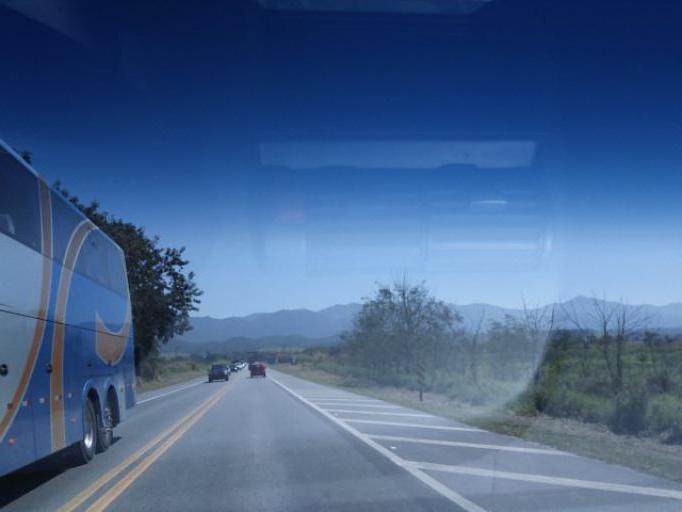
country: BR
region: Sao Paulo
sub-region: Taubate
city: Taubate
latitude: -22.9948
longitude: -45.6435
